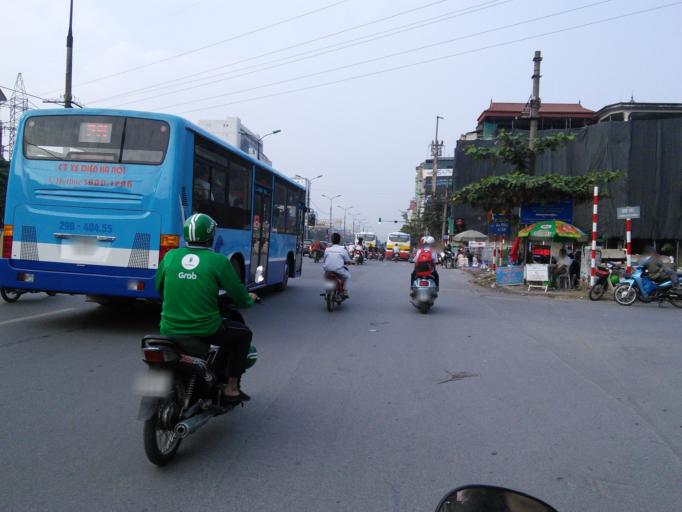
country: VN
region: Ha Noi
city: Hai BaTrung
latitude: 20.9913
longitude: 105.8412
